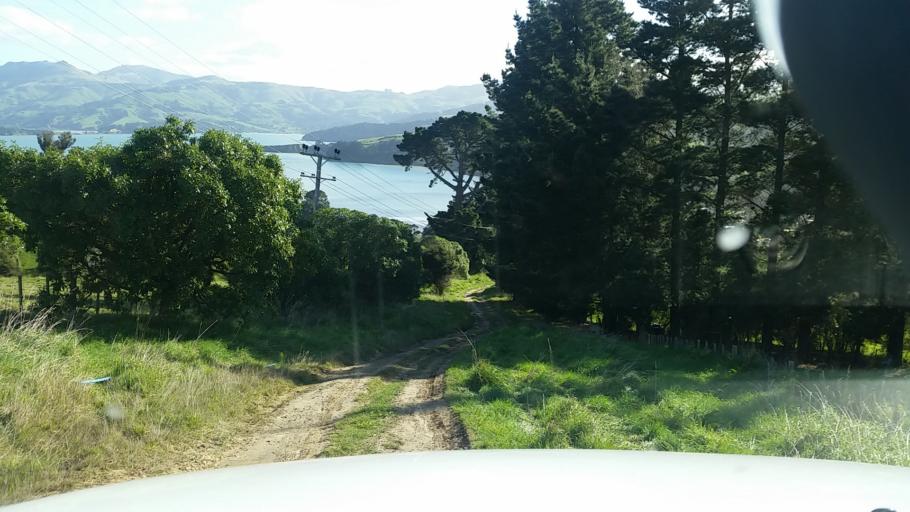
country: NZ
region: Canterbury
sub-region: Christchurch City
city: Christchurch
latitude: -43.7891
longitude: 172.9688
